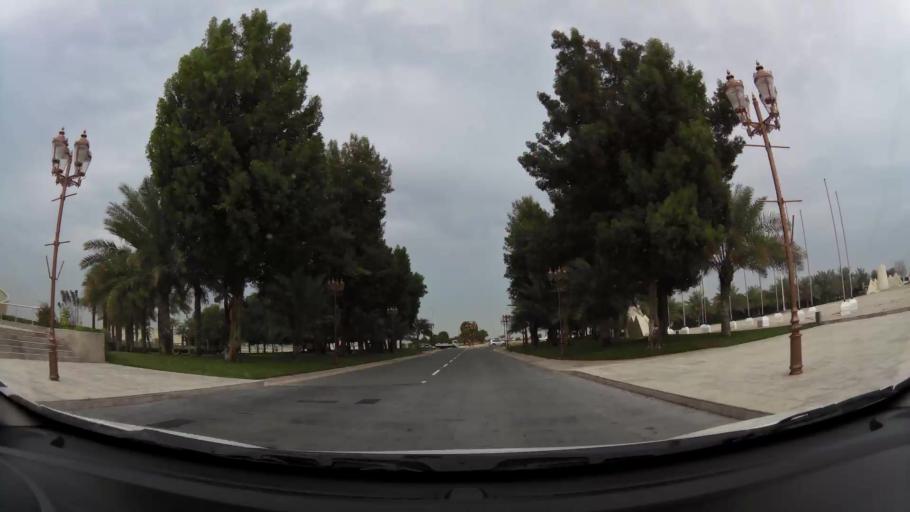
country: BH
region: Central Governorate
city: Dar Kulayb
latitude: 26.0714
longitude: 50.5277
